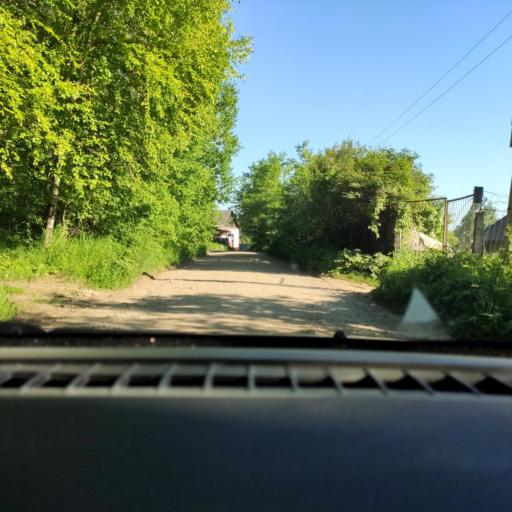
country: RU
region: Perm
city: Overyata
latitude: 58.1215
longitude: 55.8814
